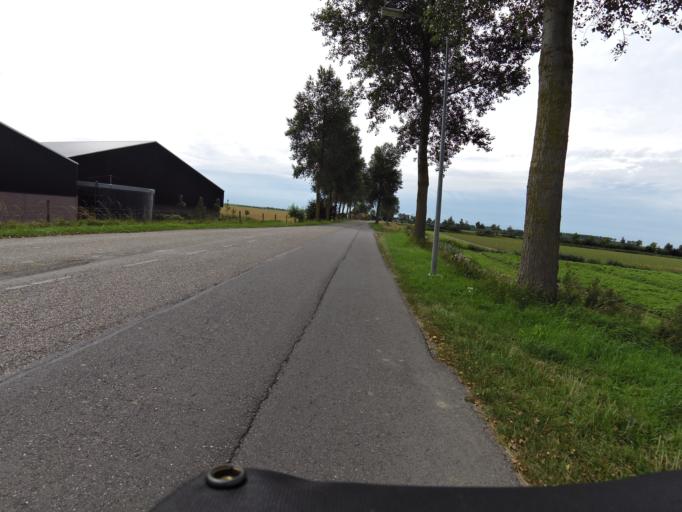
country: NL
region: South Holland
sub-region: Gemeente Goeree-Overflakkee
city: Middelharnis
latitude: 51.7079
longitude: 4.1575
